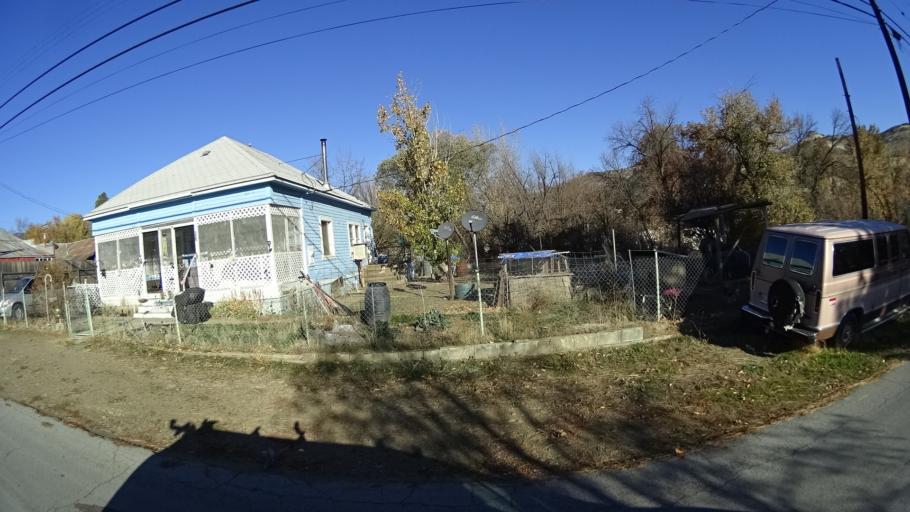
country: US
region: California
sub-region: Siskiyou County
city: Montague
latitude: 41.9093
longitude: -122.5578
